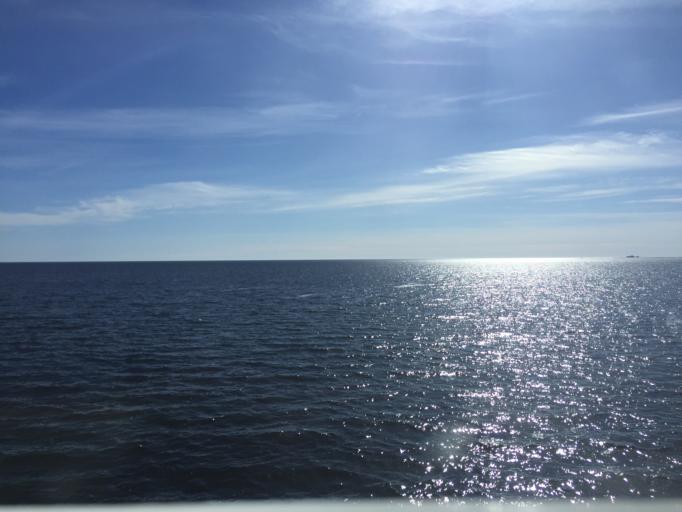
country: EE
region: Laeaene
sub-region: Haapsalu linn
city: Haapsalu
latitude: 58.5759
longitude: 23.4699
